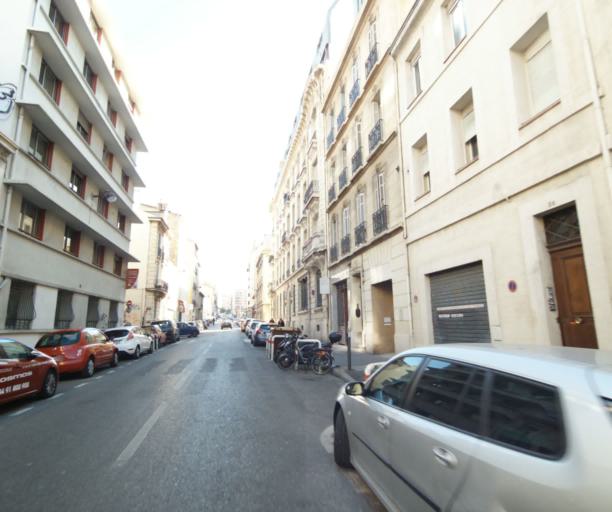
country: FR
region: Provence-Alpes-Cote d'Azur
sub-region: Departement des Bouches-du-Rhone
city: Marseille 06
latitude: 43.2857
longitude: 5.3864
